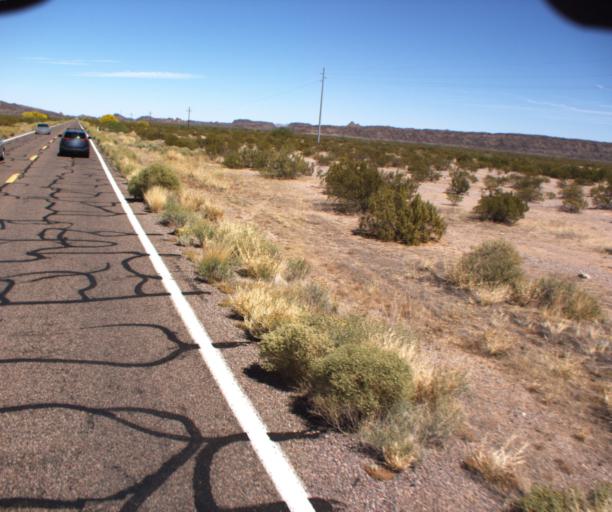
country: US
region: Arizona
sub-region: Pima County
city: Ajo
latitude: 32.5086
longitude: -112.8809
